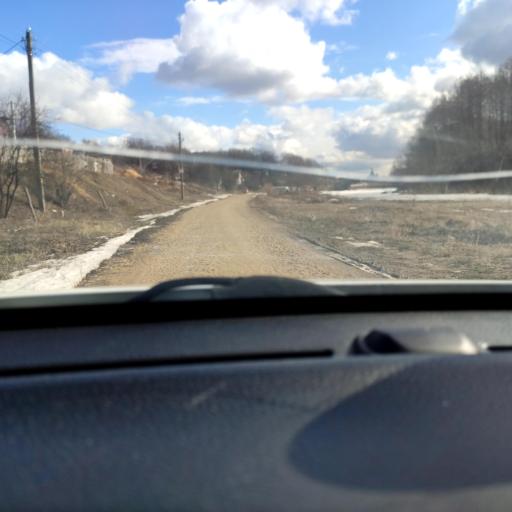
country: RU
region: Voronezj
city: Novaya Usman'
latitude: 51.6891
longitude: 39.3847
